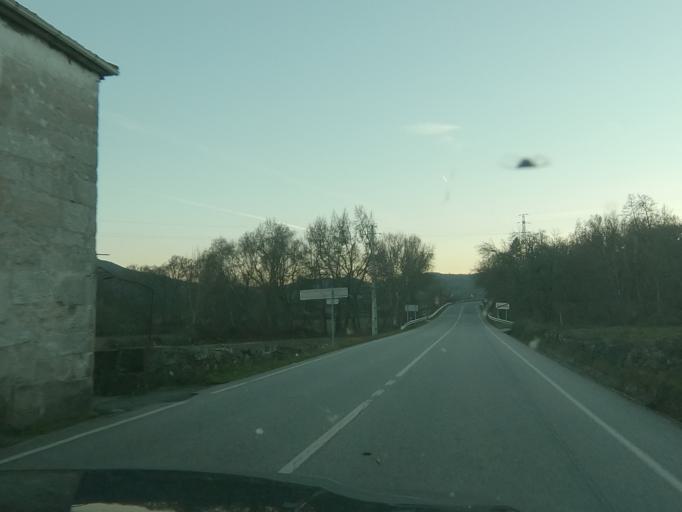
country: PT
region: Vila Real
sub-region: Vila Pouca de Aguiar
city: Vila Pouca de Aguiar
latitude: 41.4298
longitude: -7.6809
